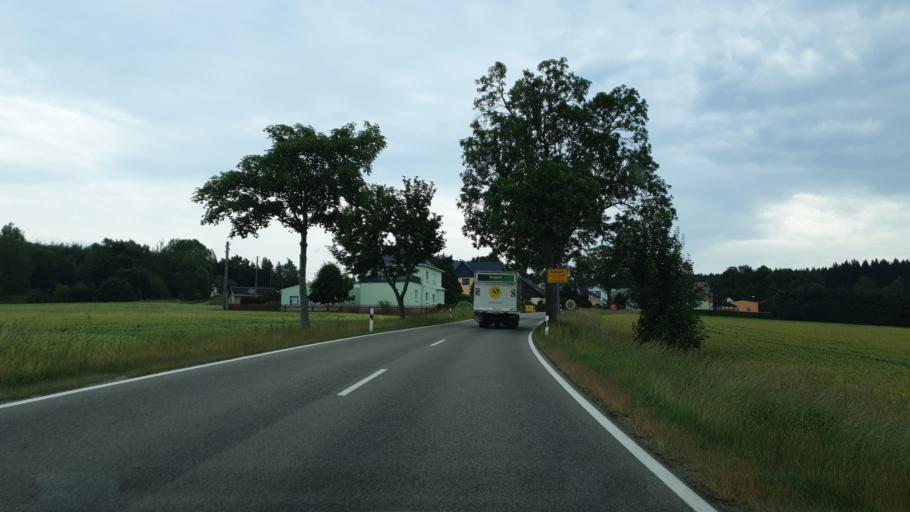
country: DE
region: Saxony
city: Auerbach
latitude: 50.4905
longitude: 12.4297
